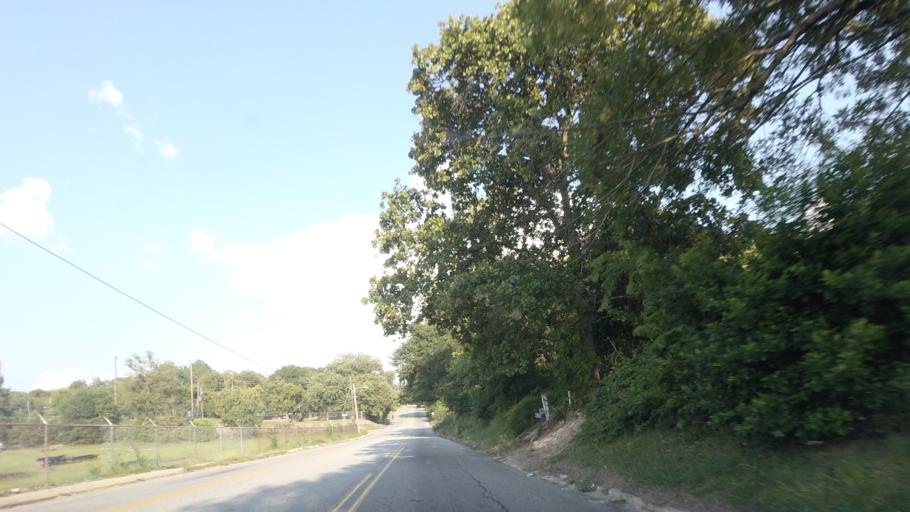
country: US
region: Georgia
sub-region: Bibb County
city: Macon
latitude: 32.8391
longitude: -83.6714
